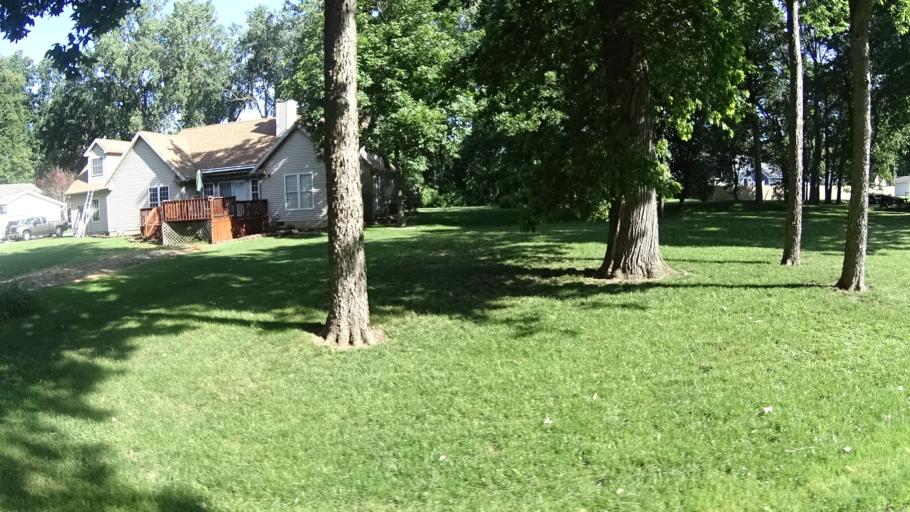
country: US
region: Ohio
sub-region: Erie County
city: Sandusky
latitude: 41.4647
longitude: -82.8240
